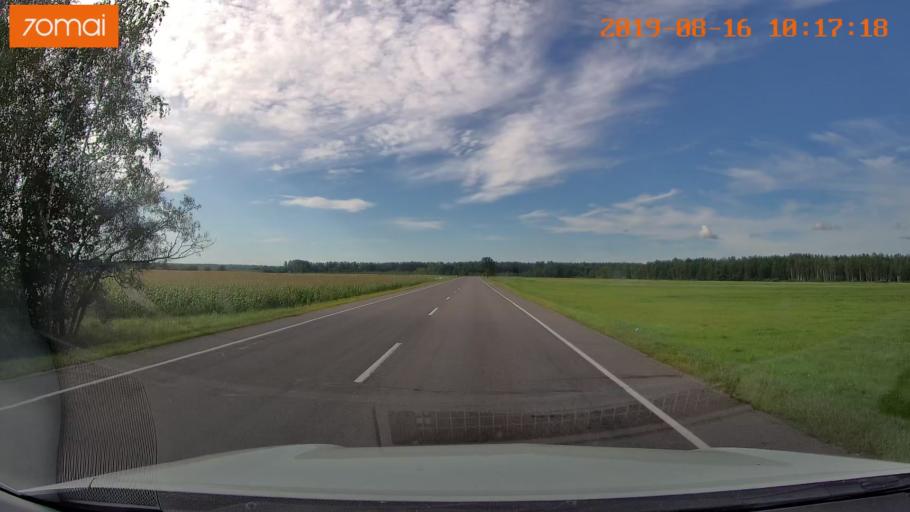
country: BY
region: Mogilev
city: Asipovichy
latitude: 53.3124
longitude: 28.7130
